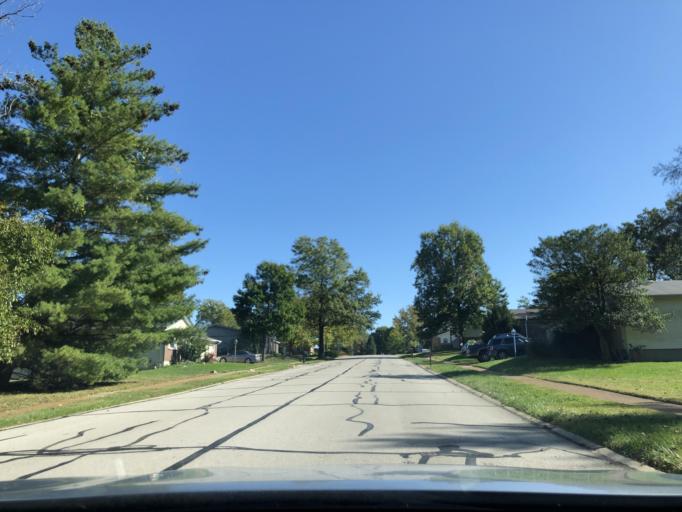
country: US
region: Missouri
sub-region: Saint Louis County
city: Concord
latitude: 38.4932
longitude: -90.3603
